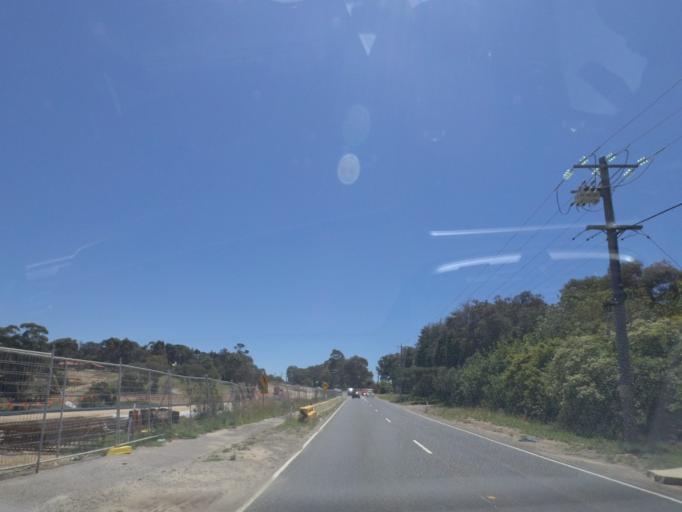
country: AU
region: Victoria
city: Plenty
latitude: -37.6674
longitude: 145.1240
